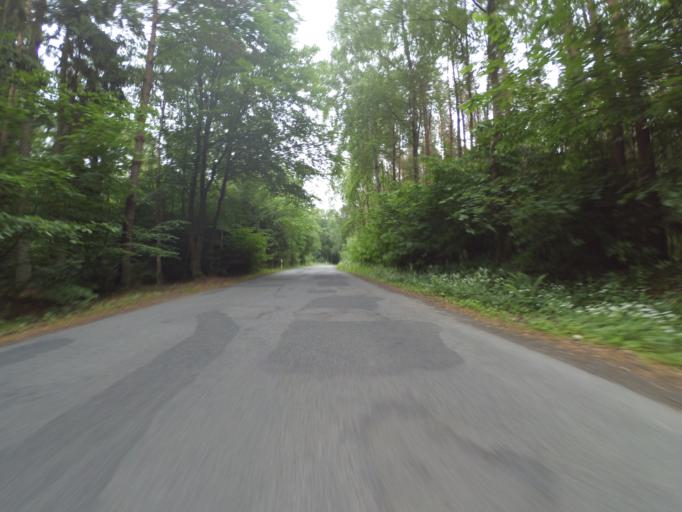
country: DE
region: Mecklenburg-Vorpommern
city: Demen
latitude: 53.6373
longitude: 11.8276
